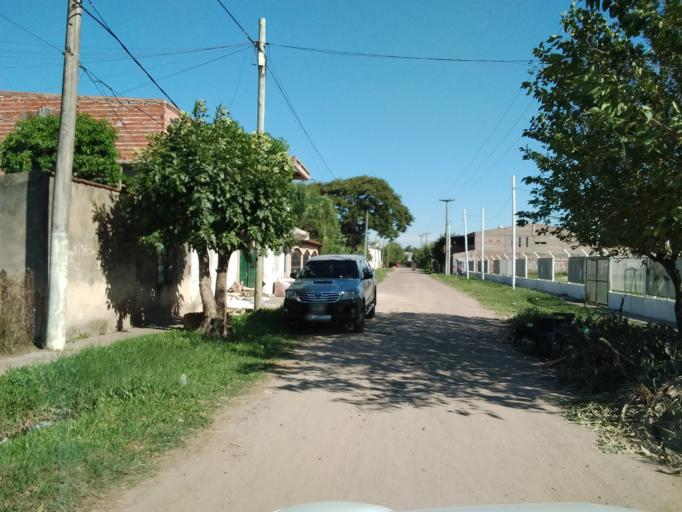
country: AR
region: Corrientes
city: Corrientes
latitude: -27.4844
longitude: -58.8059
